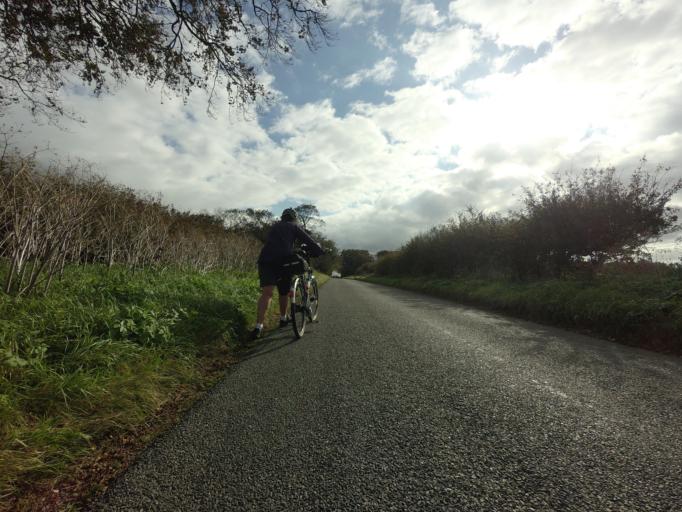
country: GB
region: England
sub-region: Norfolk
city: Heacham
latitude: 52.9193
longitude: 0.5420
